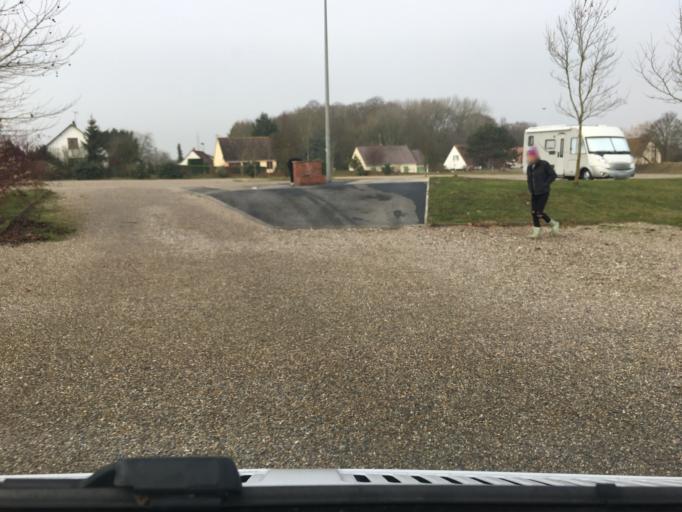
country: FR
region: Picardie
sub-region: Departement de la Somme
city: Saint-Valery-sur-Somme
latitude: 50.1828
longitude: 1.6289
